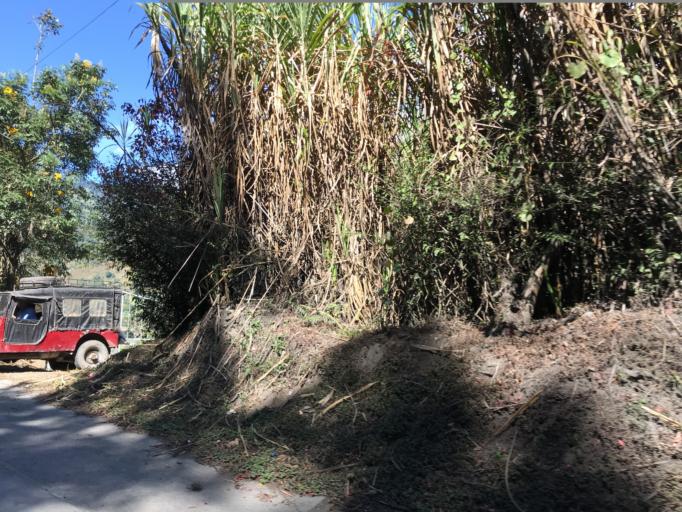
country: CO
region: Tolima
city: Cajamarca
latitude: 4.4421
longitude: -75.4181
